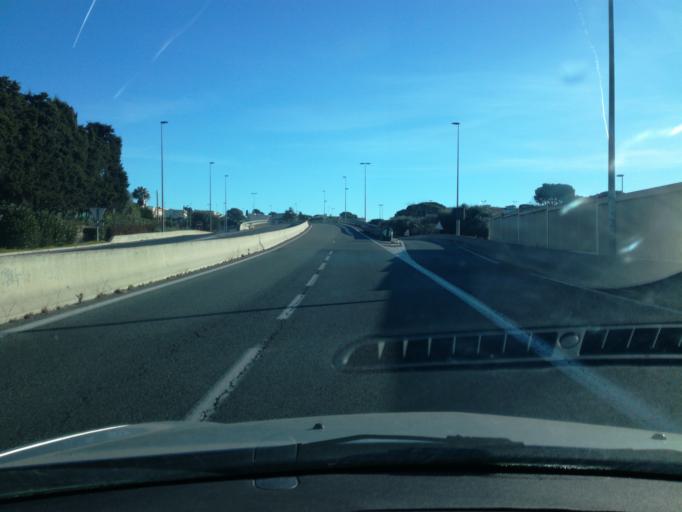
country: FR
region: Provence-Alpes-Cote d'Azur
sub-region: Departement des Alpes-Maritimes
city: Antibes
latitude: 43.5776
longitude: 7.1031
